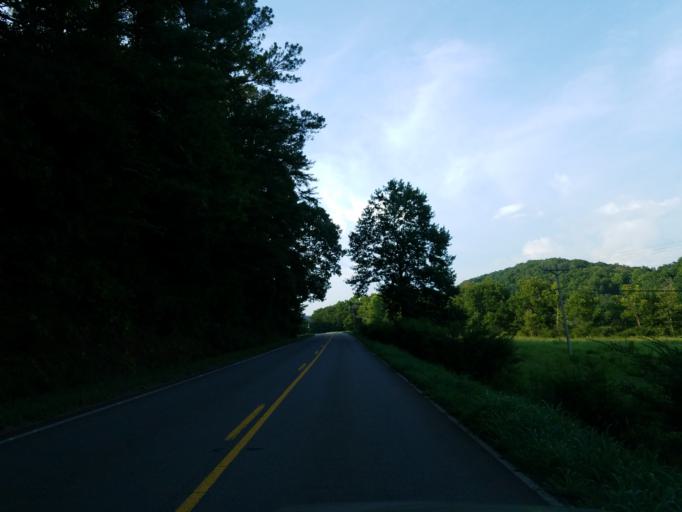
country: US
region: Georgia
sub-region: Pickens County
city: Jasper
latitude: 34.5550
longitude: -84.5395
